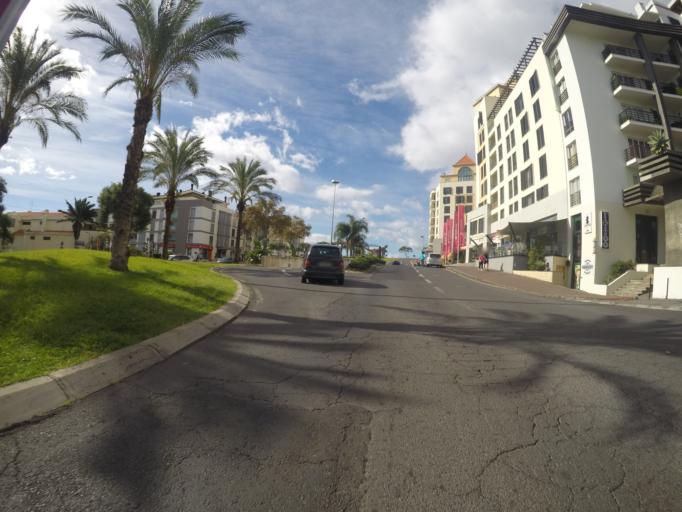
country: PT
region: Madeira
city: Camara de Lobos
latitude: 32.6357
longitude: -16.9424
